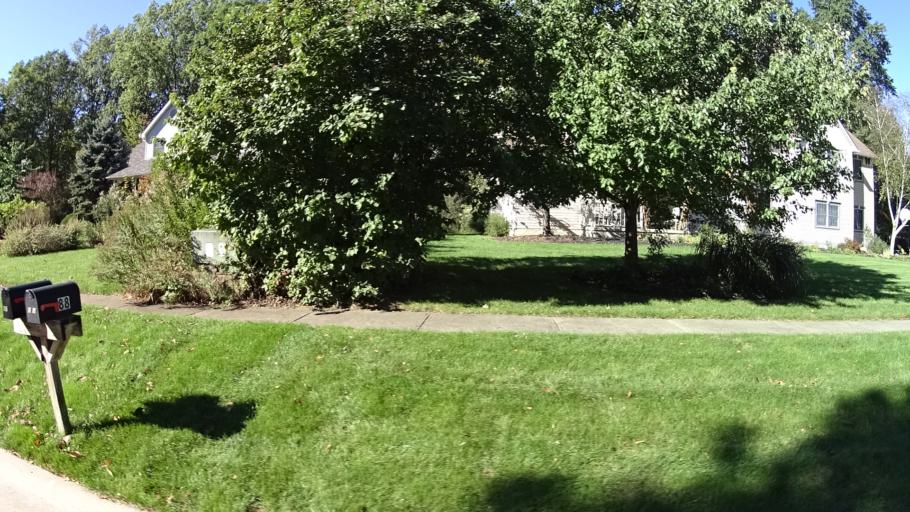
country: US
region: Ohio
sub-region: Lorain County
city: Amherst
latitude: 41.3884
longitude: -82.2481
